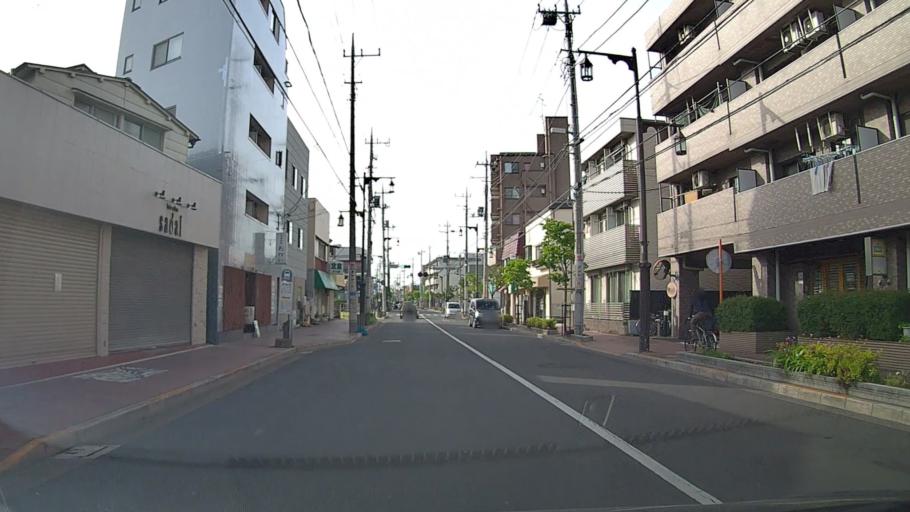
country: JP
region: Saitama
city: Soka
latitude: 35.7988
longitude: 139.7860
